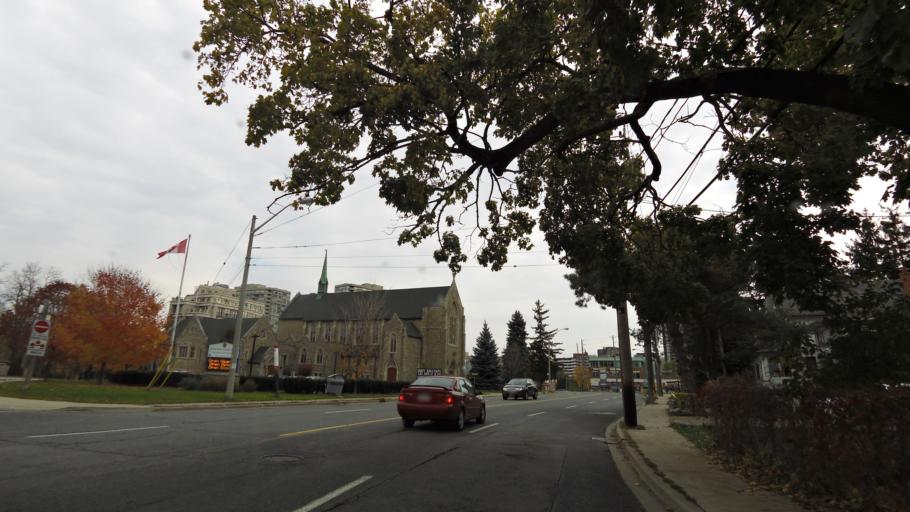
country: CA
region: Ontario
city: Etobicoke
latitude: 43.6495
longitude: -79.5311
